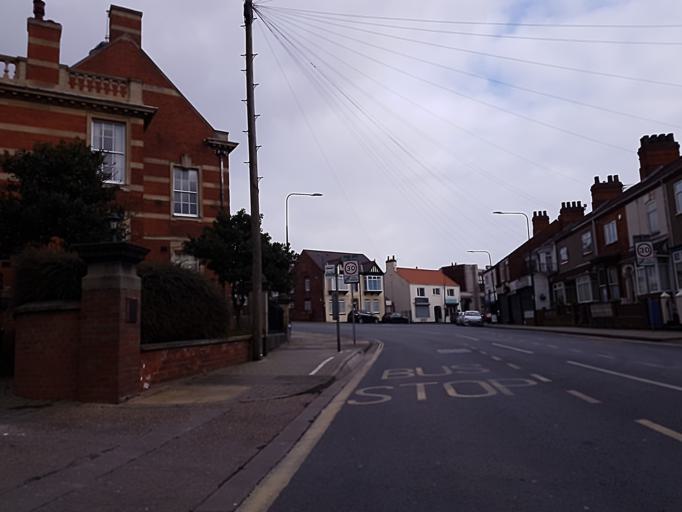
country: GB
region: England
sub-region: North East Lincolnshire
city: Cleethorpes
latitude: 53.5576
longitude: -0.0280
